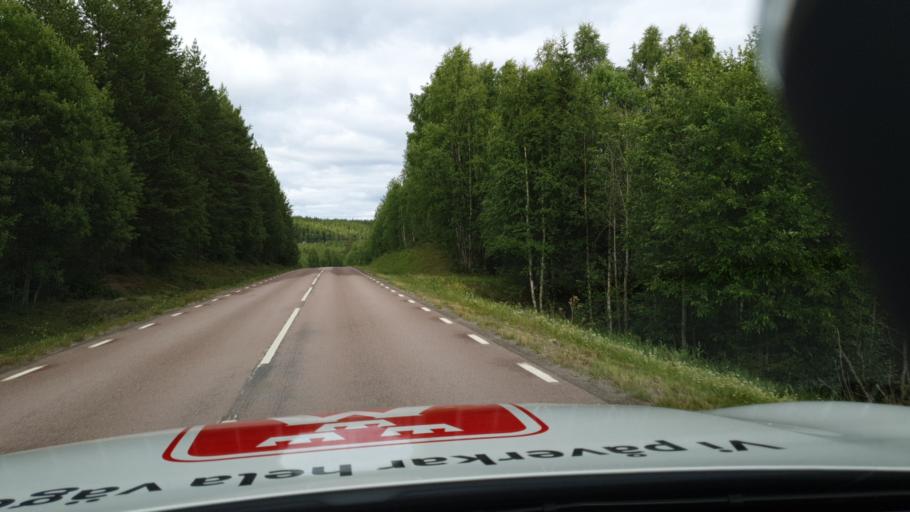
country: SE
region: Vaesternorrland
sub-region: Solleftea Kommun
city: As
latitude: 63.5958
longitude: 16.2508
